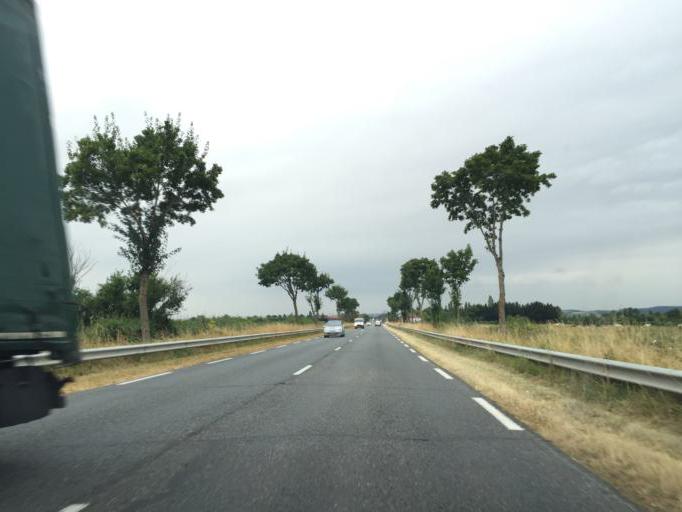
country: FR
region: Auvergne
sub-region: Departement de l'Allier
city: Brout-Vernet
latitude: 46.1776
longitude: 3.2497
